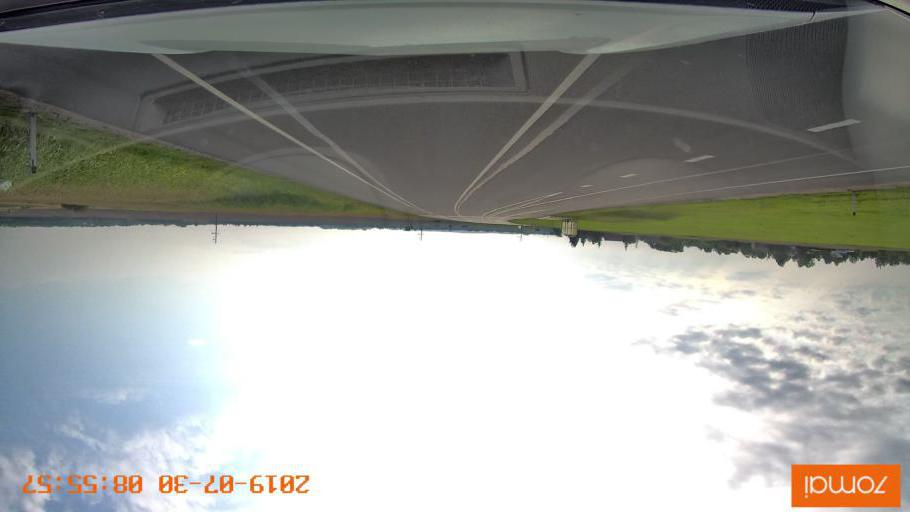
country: RU
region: Kaliningrad
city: Gusev
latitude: 54.5988
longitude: 22.0642
